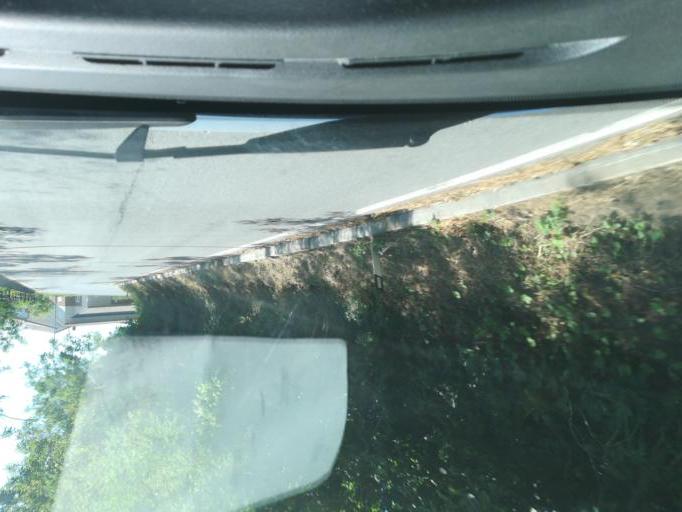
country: IT
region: The Marches
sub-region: Provincia di Macerata
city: San Ginesio
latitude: 43.1067
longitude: 13.3274
